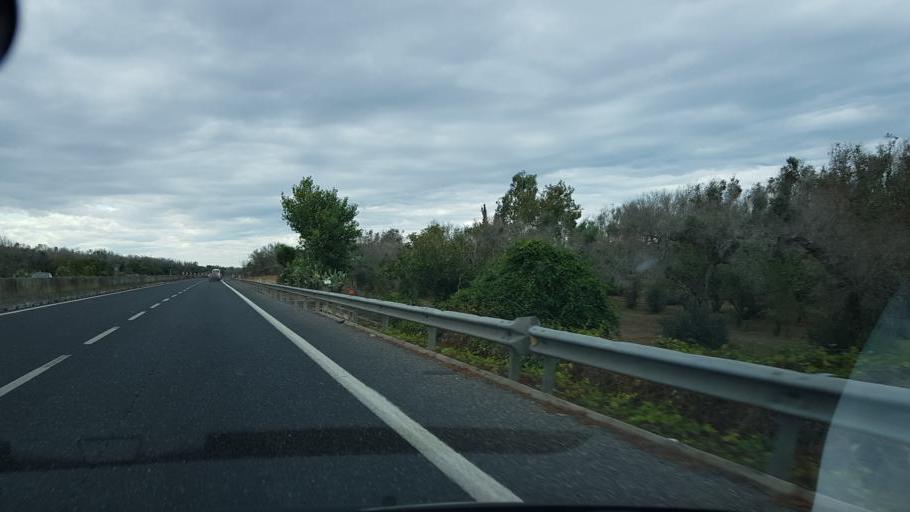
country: IT
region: Apulia
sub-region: Provincia di Brindisi
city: Torchiarolo
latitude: 40.4657
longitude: 18.0551
